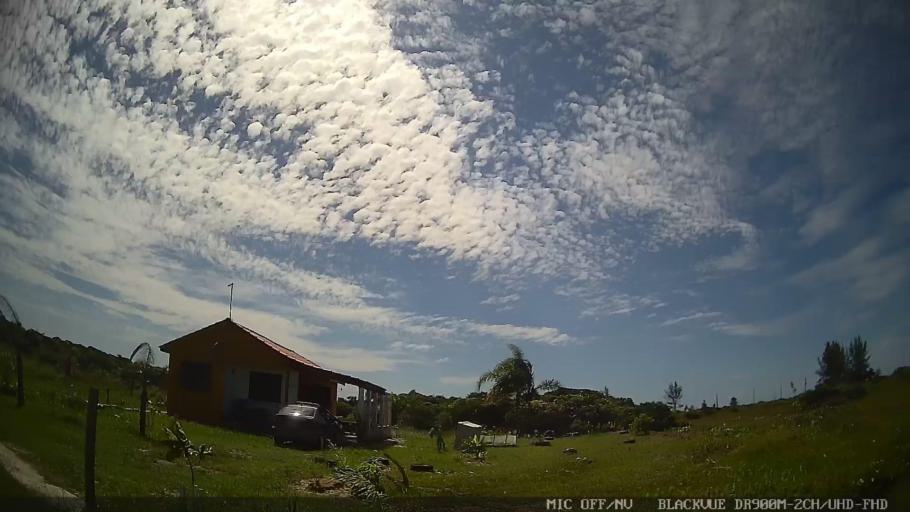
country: BR
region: Sao Paulo
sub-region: Iguape
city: Iguape
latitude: -24.8063
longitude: -47.6406
